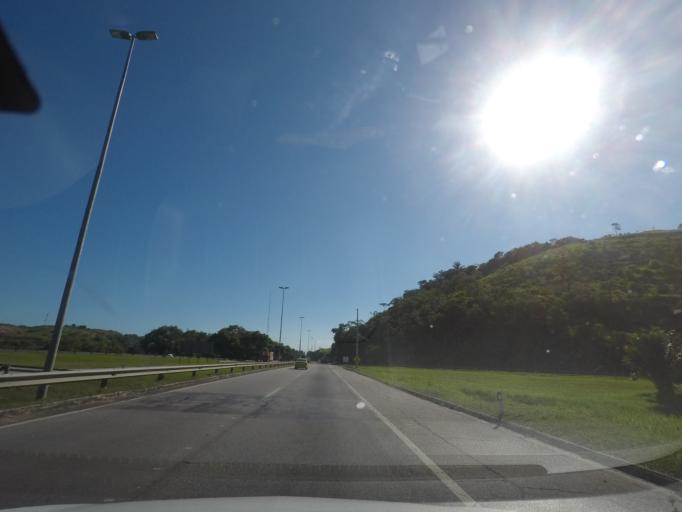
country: BR
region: Rio de Janeiro
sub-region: Guapimirim
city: Guapimirim
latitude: -22.6575
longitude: -43.0895
